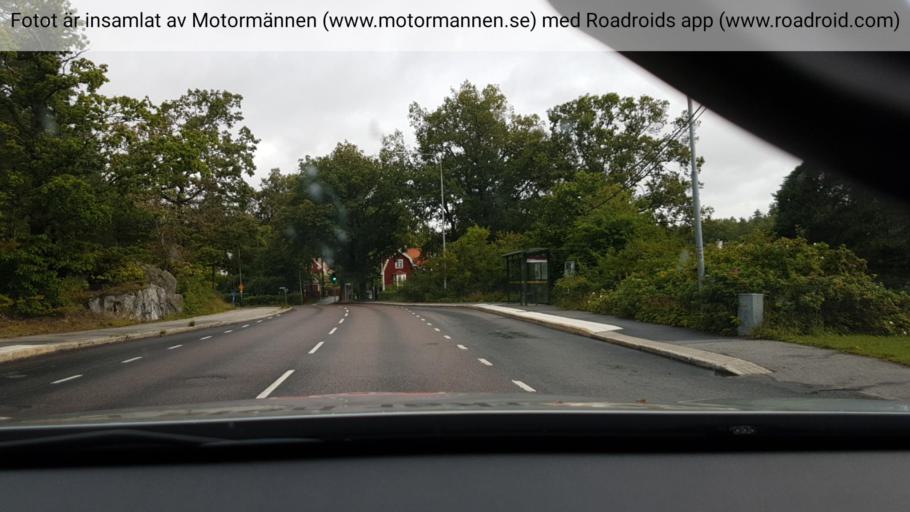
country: SE
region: Stockholm
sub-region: Lidingo
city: Brevik
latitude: 59.3477
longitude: 18.1747
